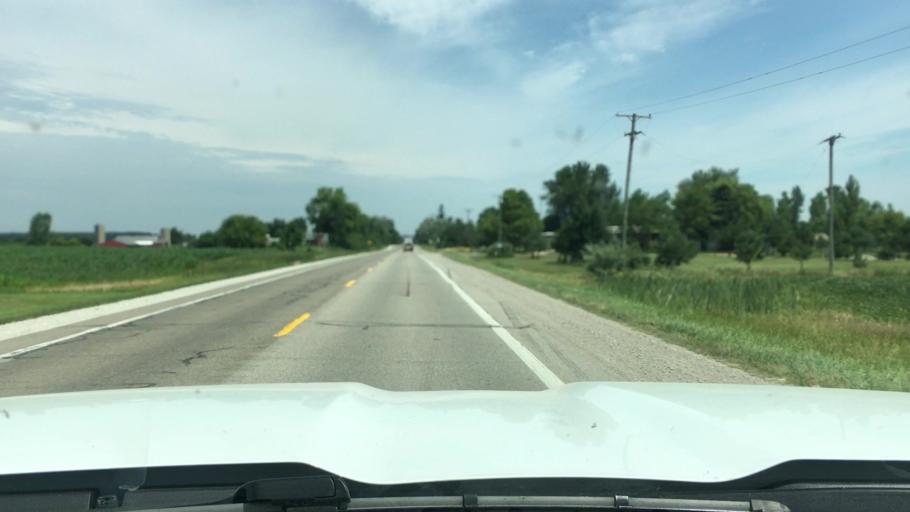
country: US
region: Michigan
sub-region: Sanilac County
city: Brown City
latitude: 43.1948
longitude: -83.0767
